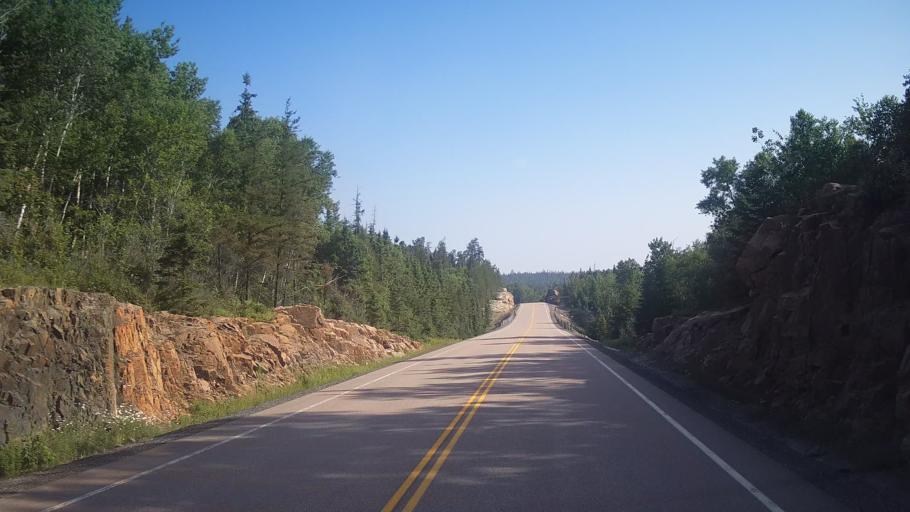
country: CA
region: Ontario
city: Rayside-Balfour
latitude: 46.9847
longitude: -81.6343
